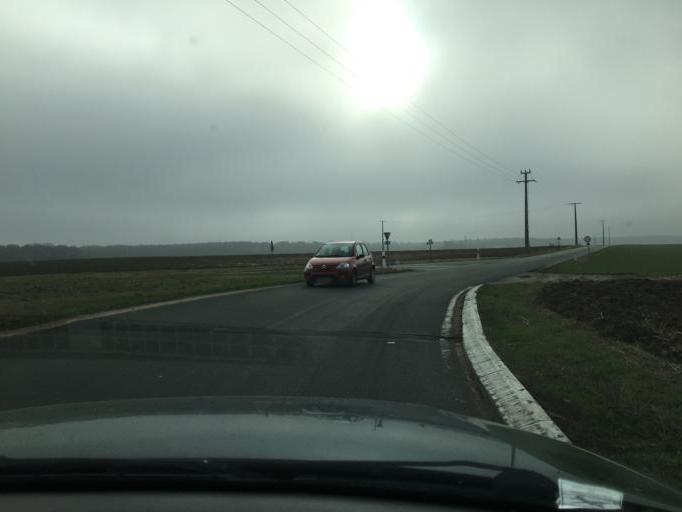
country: FR
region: Centre
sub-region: Departement du Loiret
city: Gidy
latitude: 47.9768
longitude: 1.8420
